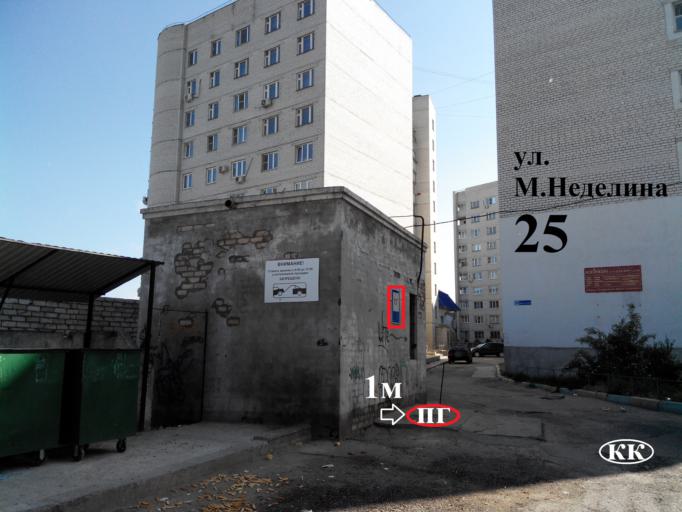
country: RU
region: Voronezj
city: Voronezh
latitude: 51.6433
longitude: 39.1639
